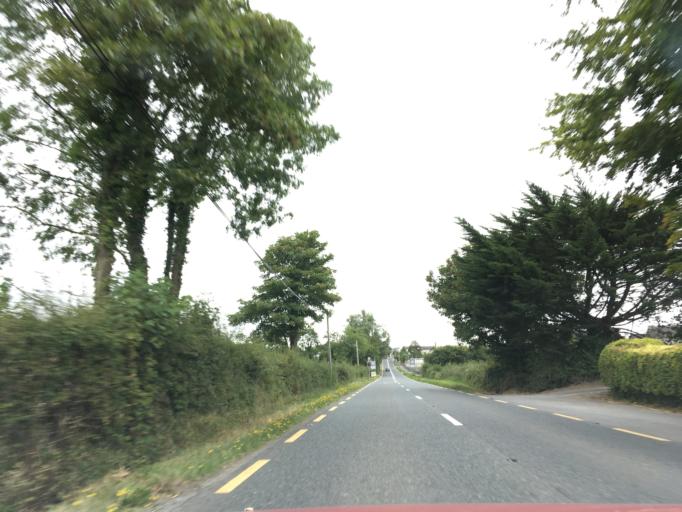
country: IE
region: Munster
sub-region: South Tipperary
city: Cluain Meala
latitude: 52.4155
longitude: -7.7592
